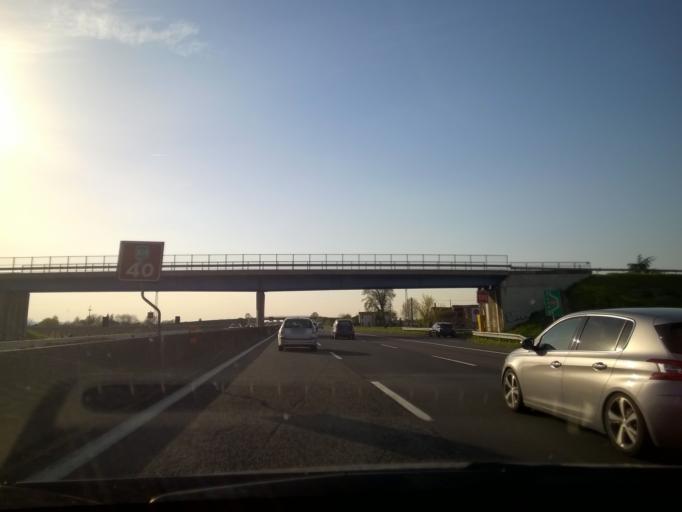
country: IT
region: Emilia-Romagna
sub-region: Provincia di Bologna
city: Castel Guelfo di Bologna
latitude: 44.4002
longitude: 11.6917
